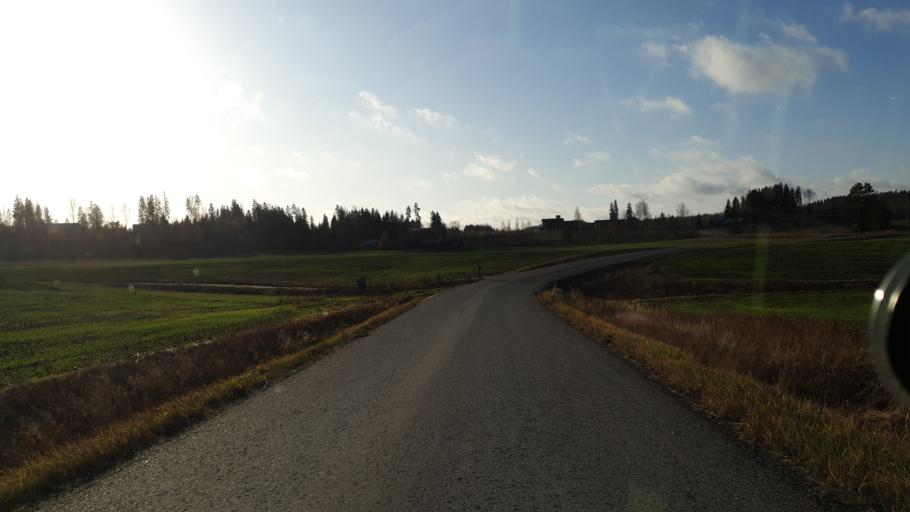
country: FI
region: Uusimaa
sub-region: Helsinki
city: Lohja
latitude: 60.2320
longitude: 24.1680
